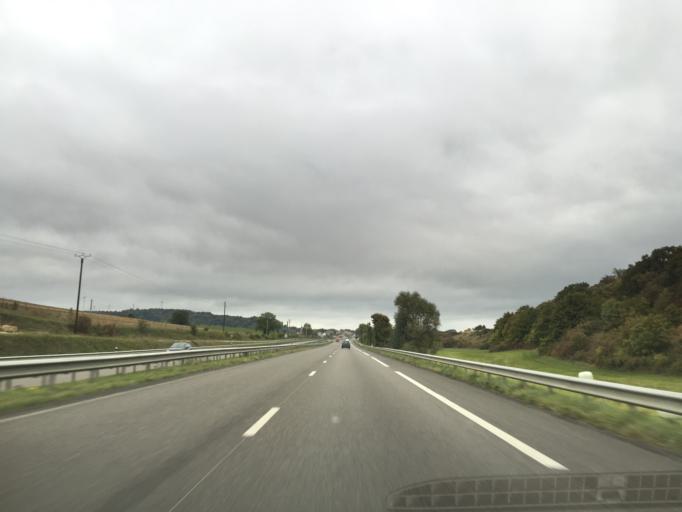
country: FR
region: Lorraine
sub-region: Departement de la Meuse
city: Vacon
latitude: 48.6956
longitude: 5.5460
